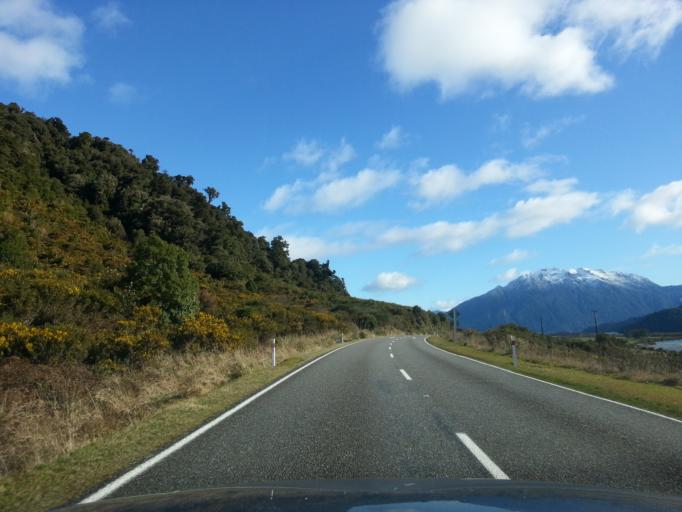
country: NZ
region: West Coast
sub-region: Grey District
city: Greymouth
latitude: -42.7354
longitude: 171.4379
